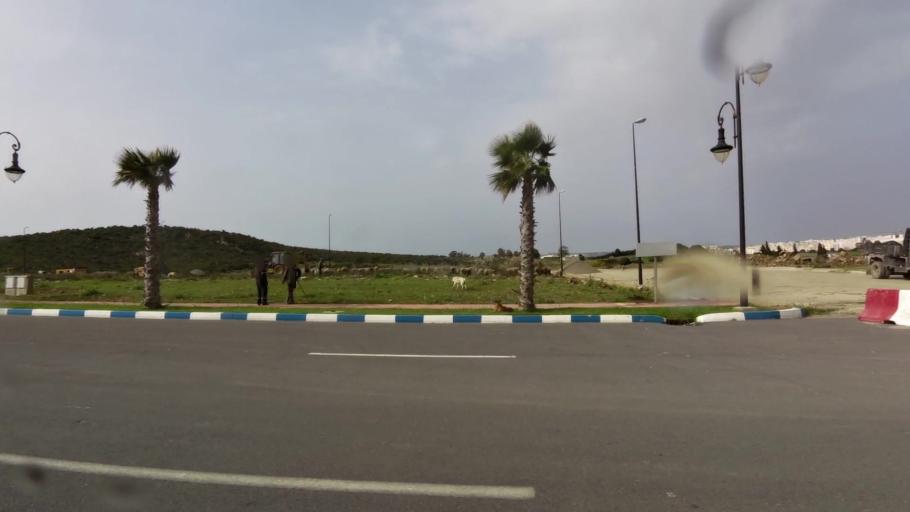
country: MA
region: Tanger-Tetouan
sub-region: Tanger-Assilah
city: Boukhalef
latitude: 35.6970
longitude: -5.9230
